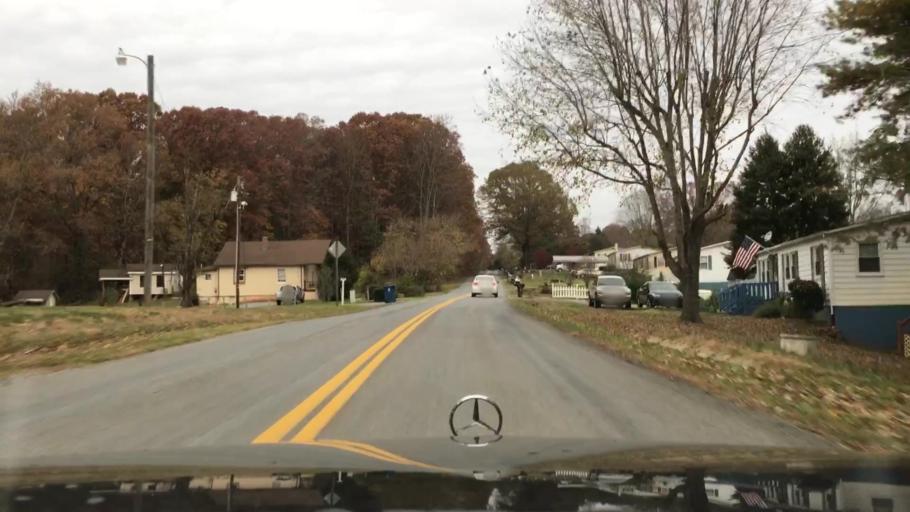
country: US
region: Virginia
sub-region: Campbell County
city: Timberlake
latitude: 37.2911
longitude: -79.2775
